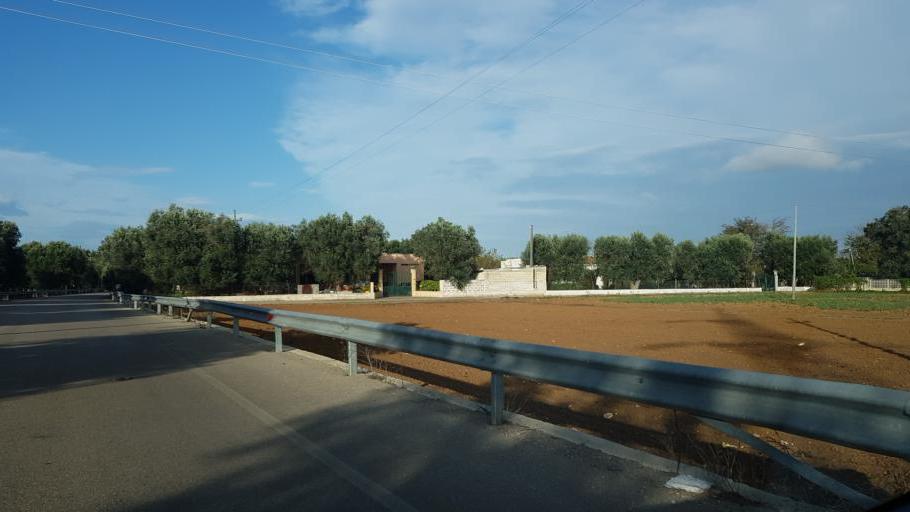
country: IT
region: Apulia
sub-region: Provincia di Brindisi
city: Oria
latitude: 40.5259
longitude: 17.6539
